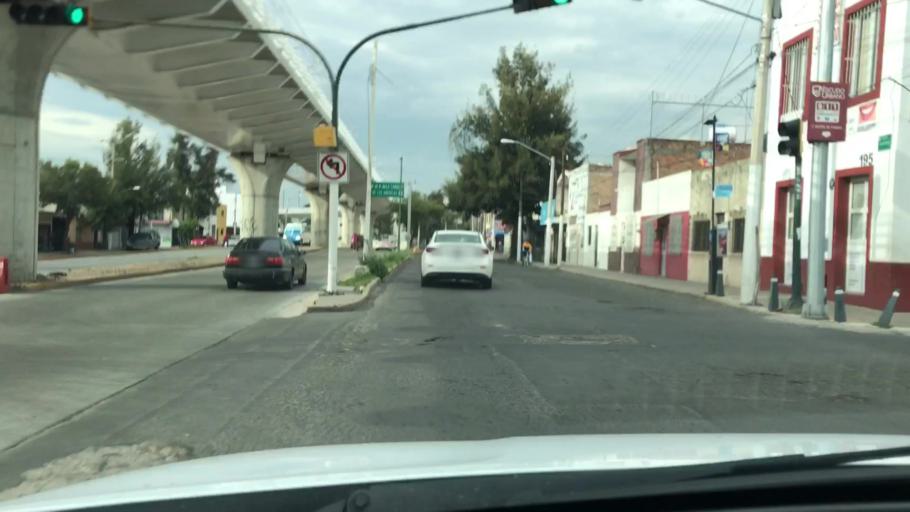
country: MX
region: Jalisco
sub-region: Zapopan
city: Zapopan
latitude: 20.7245
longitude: -103.3873
